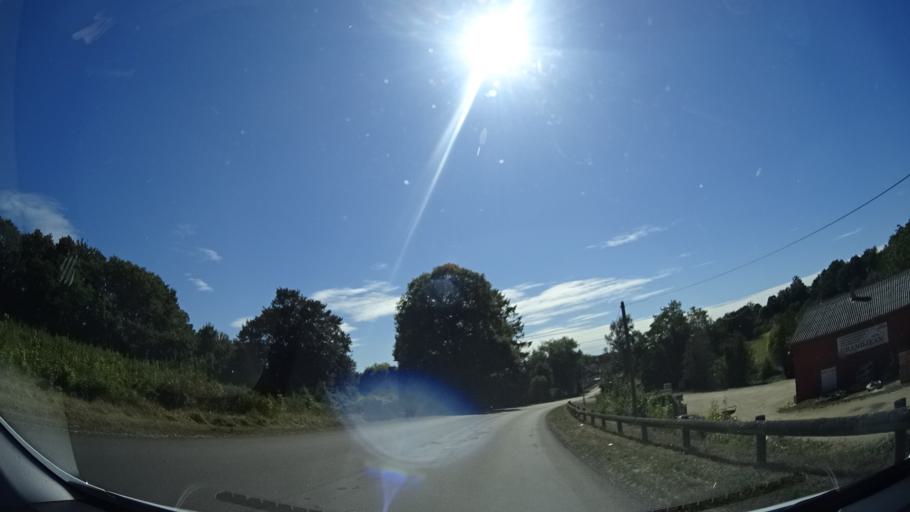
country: FR
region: Bourgogne
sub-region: Departement de l'Yonne
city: Charny
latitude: 47.9407
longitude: 3.1362
